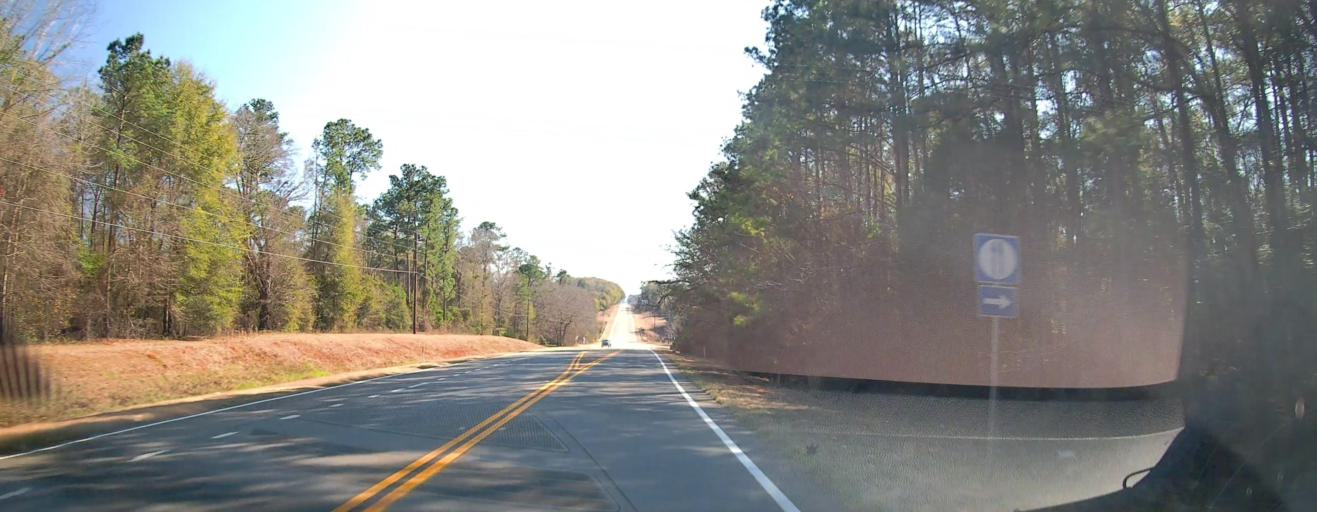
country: US
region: Georgia
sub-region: Macon County
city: Oglethorpe
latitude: 32.1979
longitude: -84.1340
